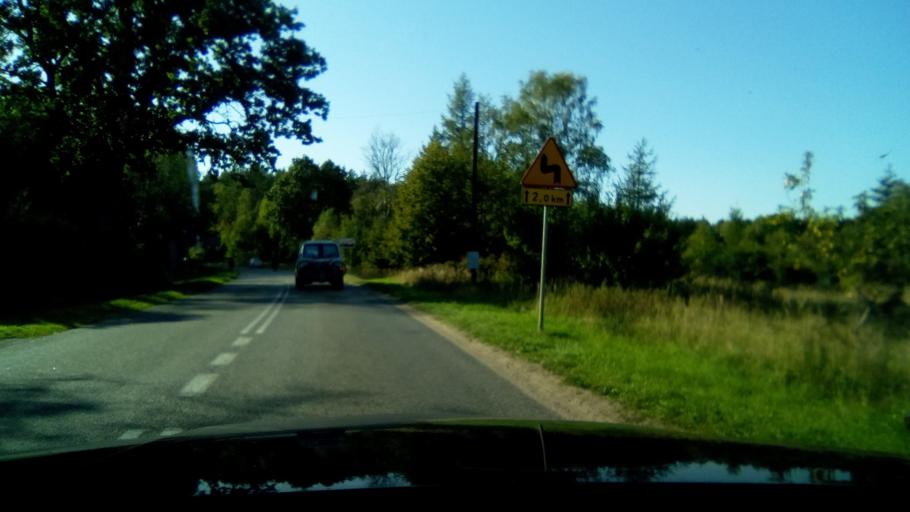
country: PL
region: West Pomeranian Voivodeship
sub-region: Powiat goleniowski
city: Przybiernow
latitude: 53.8245
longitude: 14.8316
